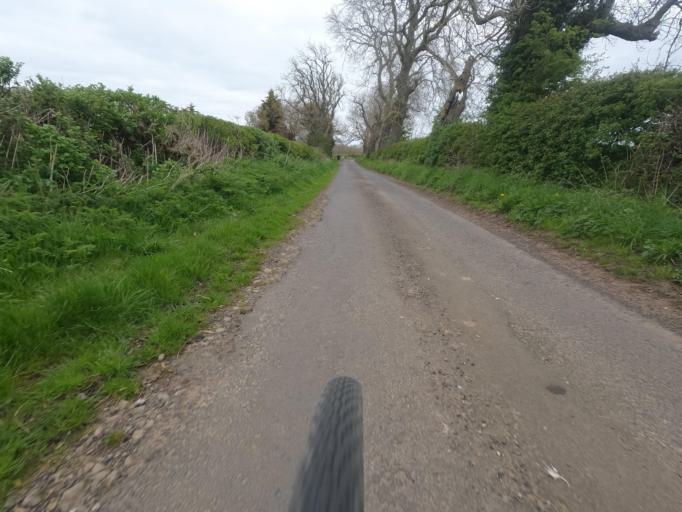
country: GB
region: England
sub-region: Northumberland
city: Meldon
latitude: 55.0702
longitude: -1.8235
